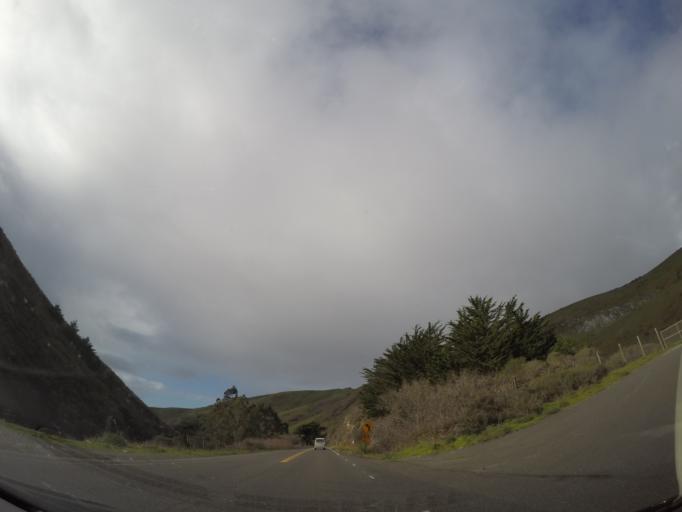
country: US
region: California
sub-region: Sonoma County
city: Bodega Bay
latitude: 38.3267
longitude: -123.0046
